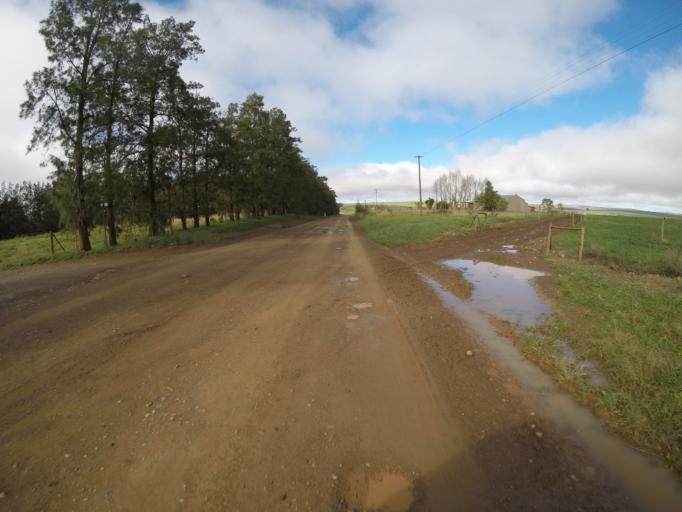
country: ZA
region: Western Cape
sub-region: Cape Winelands District Municipality
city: Ashton
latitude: -34.1416
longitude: 19.8635
